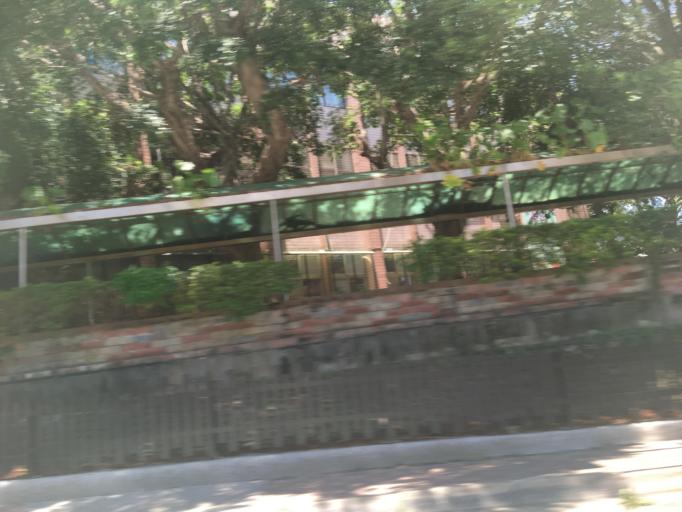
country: TW
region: Taipei
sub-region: Taipei
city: Banqiao
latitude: 25.0548
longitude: 121.4282
